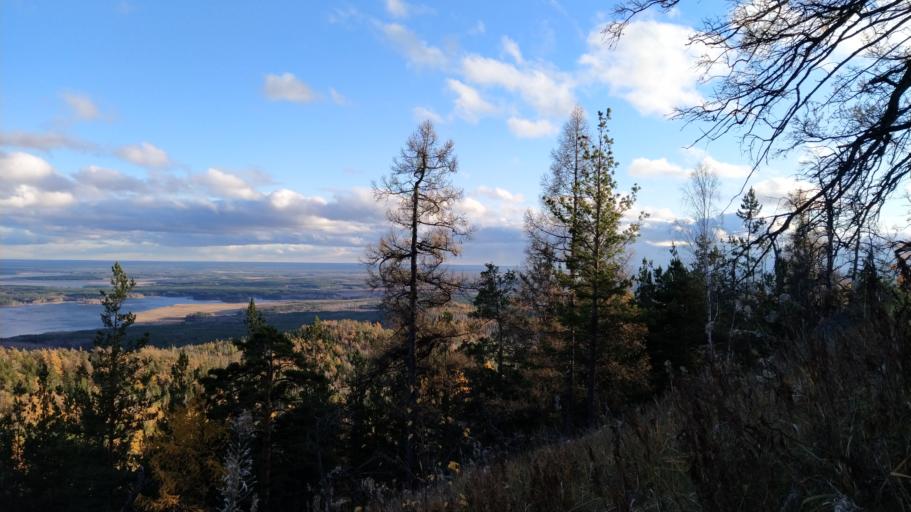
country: RU
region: Chelyabinsk
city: Kyshtym
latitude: 55.7254
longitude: 60.4431
